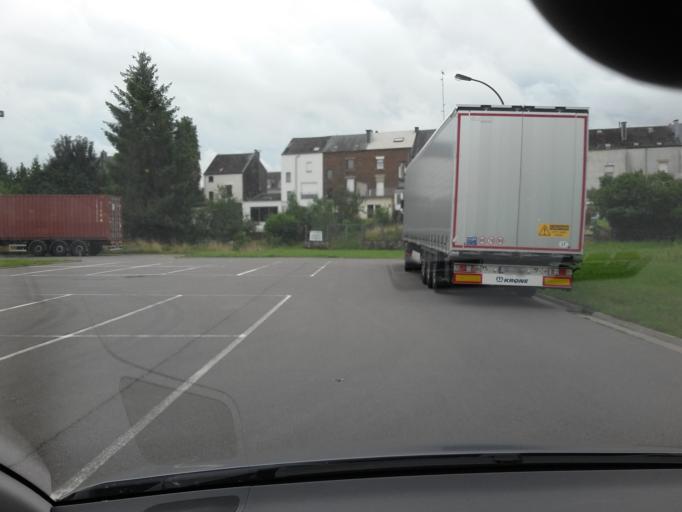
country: BE
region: Wallonia
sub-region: Province du Luxembourg
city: Arlon
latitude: 49.6788
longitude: 5.8011
